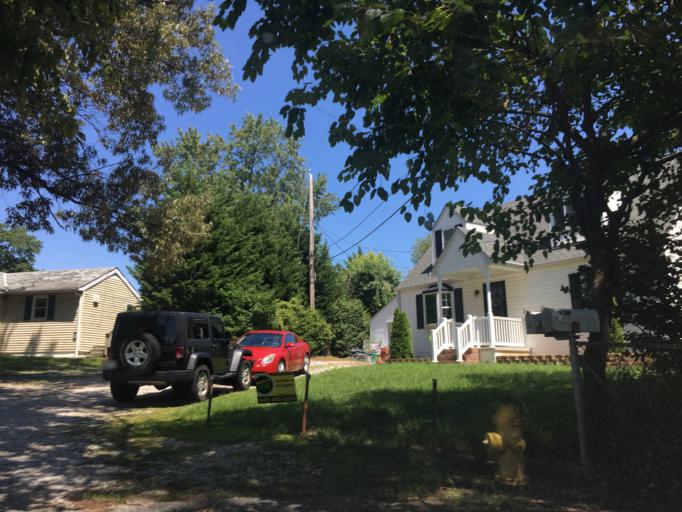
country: US
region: Maryland
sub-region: Anne Arundel County
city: Linthicum
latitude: 39.1943
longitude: -76.6538
